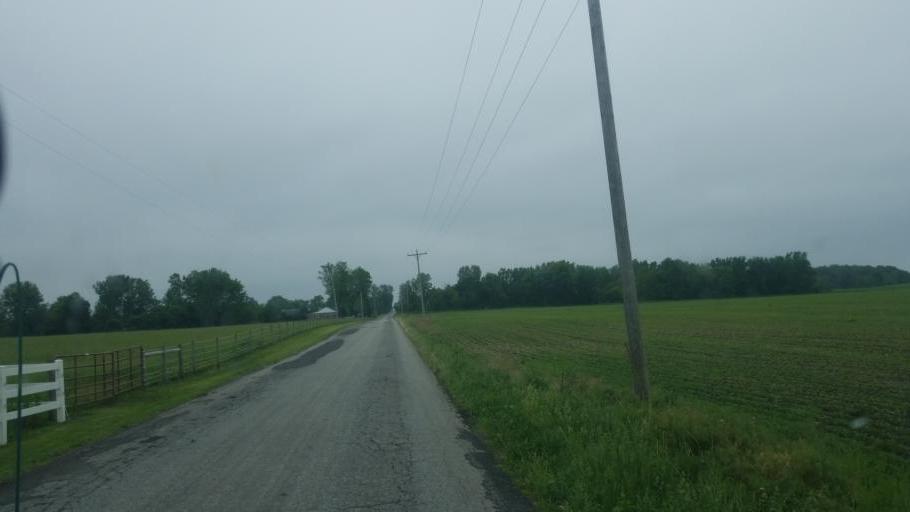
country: US
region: Indiana
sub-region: Marshall County
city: Bremen
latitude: 41.4675
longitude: -86.1177
